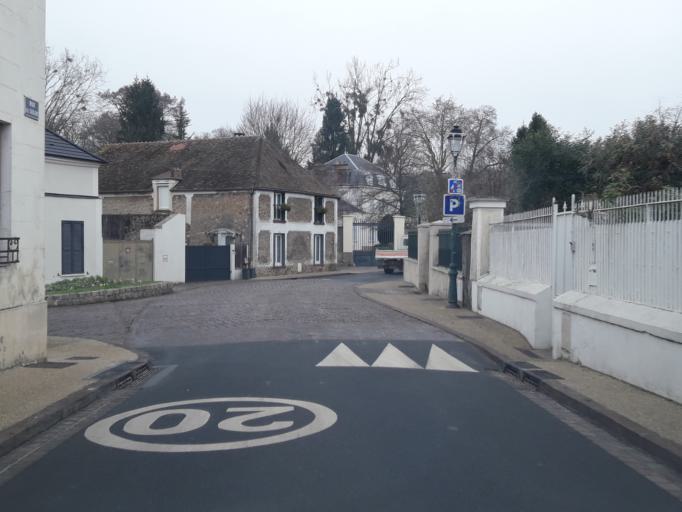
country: FR
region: Ile-de-France
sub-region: Departement de l'Essonne
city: Vert-le-Grand
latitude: 48.5737
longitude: 2.3583
